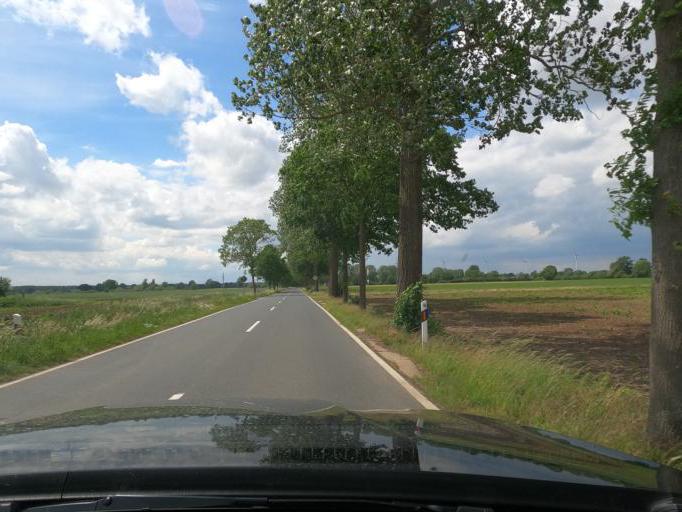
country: DE
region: Lower Saxony
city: Schwarmstedt
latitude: 52.6372
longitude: 9.5950
